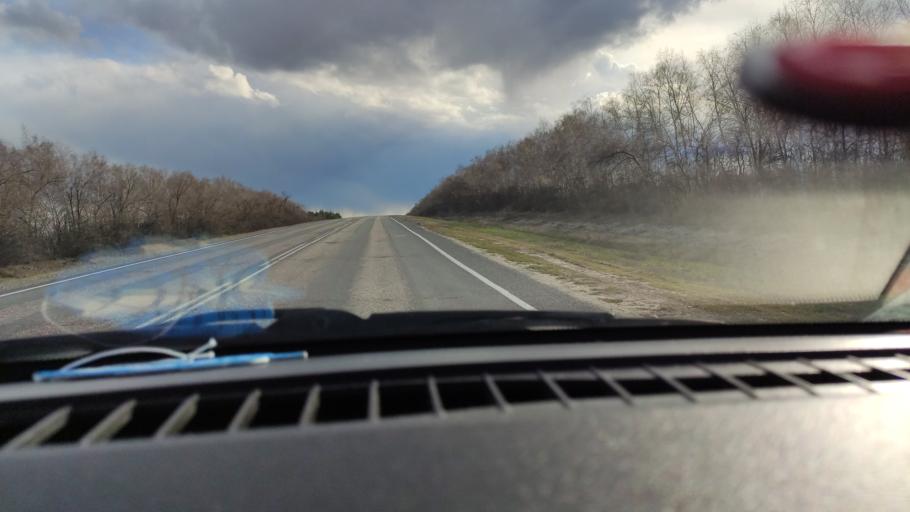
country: RU
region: Saratov
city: Sinodskoye
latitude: 51.9407
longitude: 46.5962
